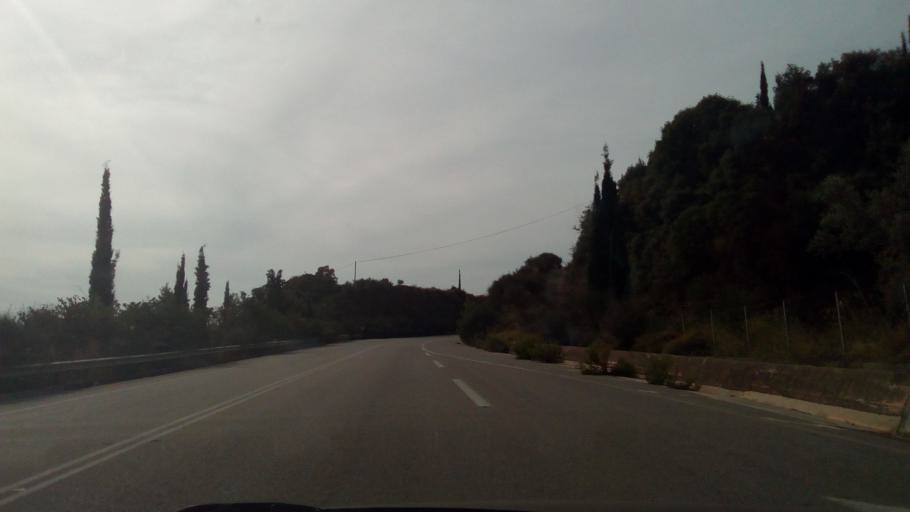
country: GR
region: West Greece
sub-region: Nomos Aitolias kai Akarnanias
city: Nafpaktos
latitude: 38.4104
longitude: 21.8399
